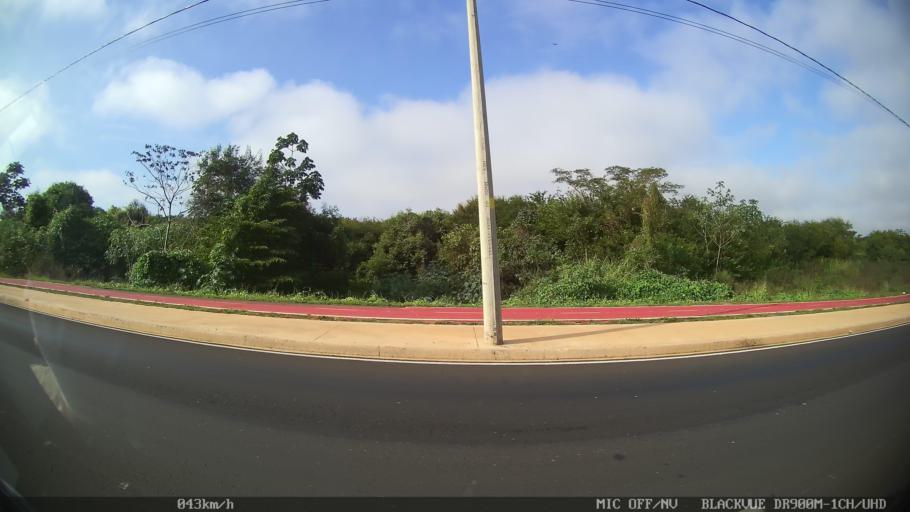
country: BR
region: Sao Paulo
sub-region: Sao Jose Do Rio Preto
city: Sao Jose do Rio Preto
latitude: -20.8073
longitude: -49.4278
